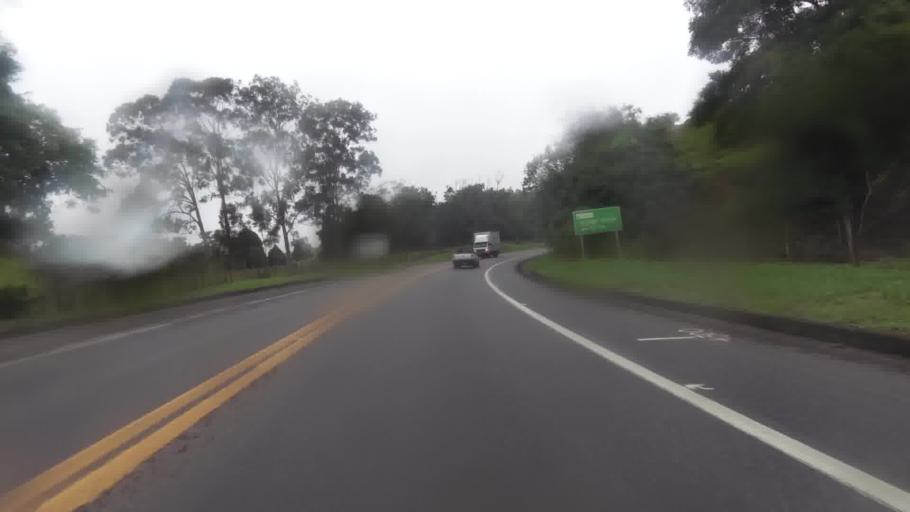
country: BR
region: Espirito Santo
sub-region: Iconha
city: Iconha
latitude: -20.7698
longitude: -40.7604
